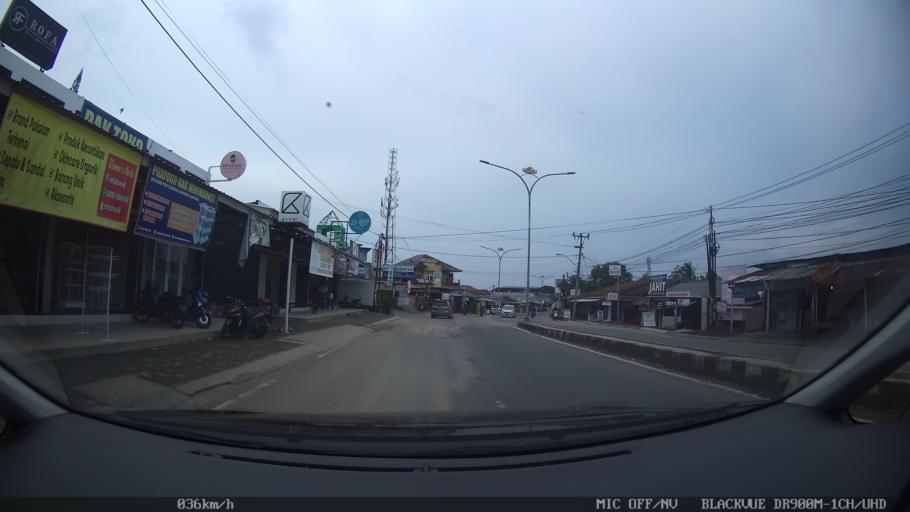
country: ID
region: Lampung
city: Kedaton
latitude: -5.3783
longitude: 105.2209
